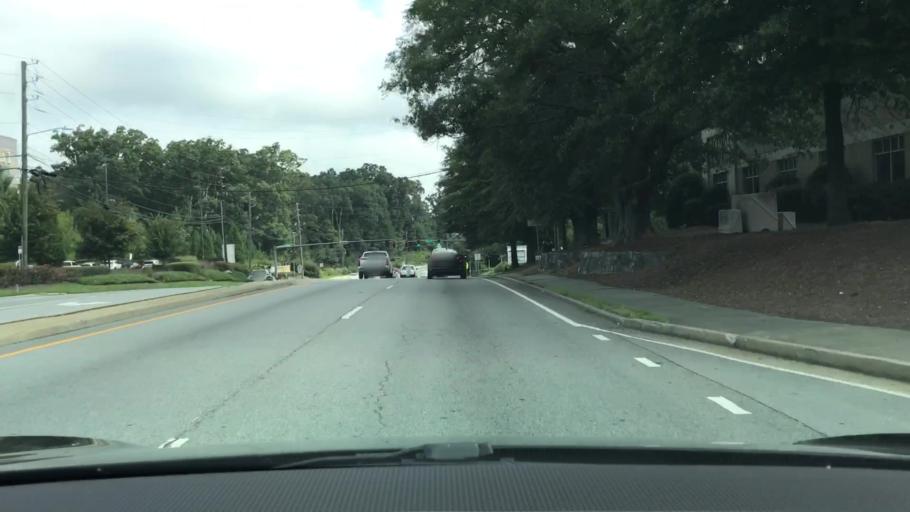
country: US
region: Georgia
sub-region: Hall County
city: Gainesville
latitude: 34.3046
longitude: -83.8110
